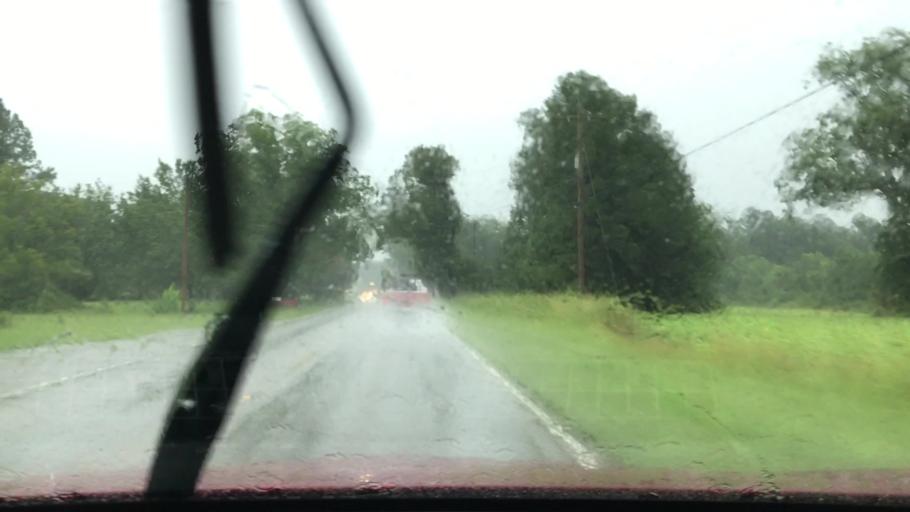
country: US
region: South Carolina
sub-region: Horry County
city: Red Hill
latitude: 33.8582
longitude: -79.0007
